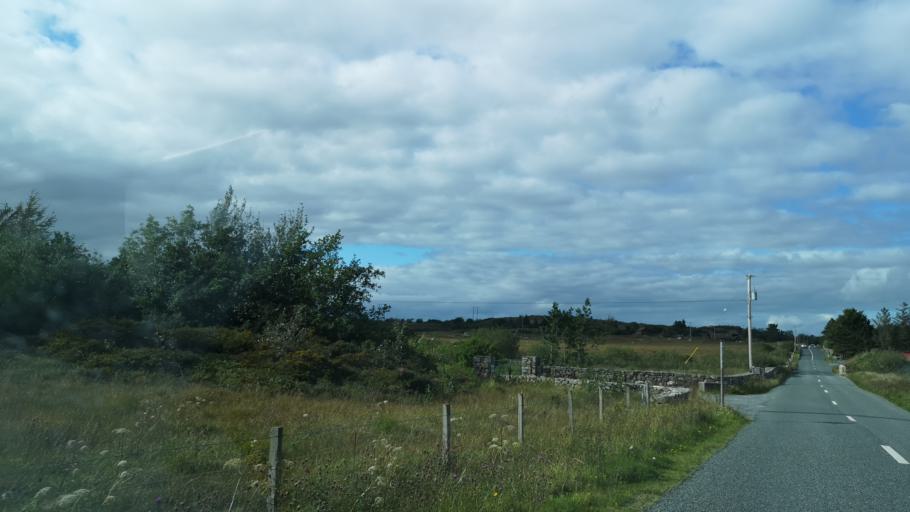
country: IE
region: Connaught
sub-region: County Galway
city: Bearna
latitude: 53.2871
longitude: -9.1635
